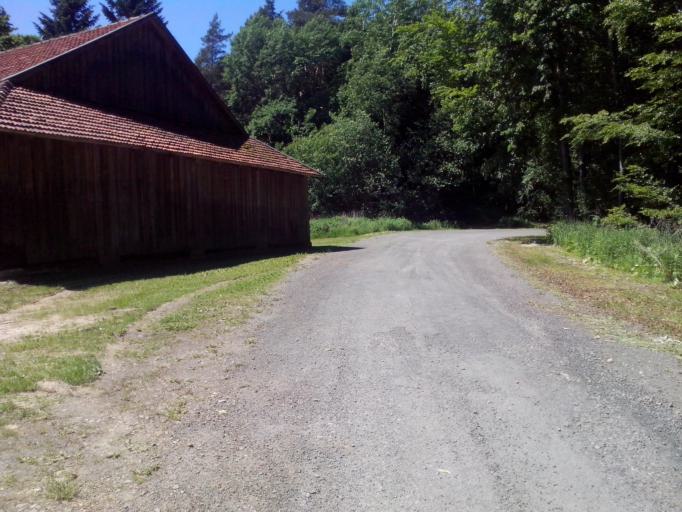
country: PL
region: Subcarpathian Voivodeship
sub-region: Powiat krosnienski
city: Leki
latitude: 49.8357
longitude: 21.6609
